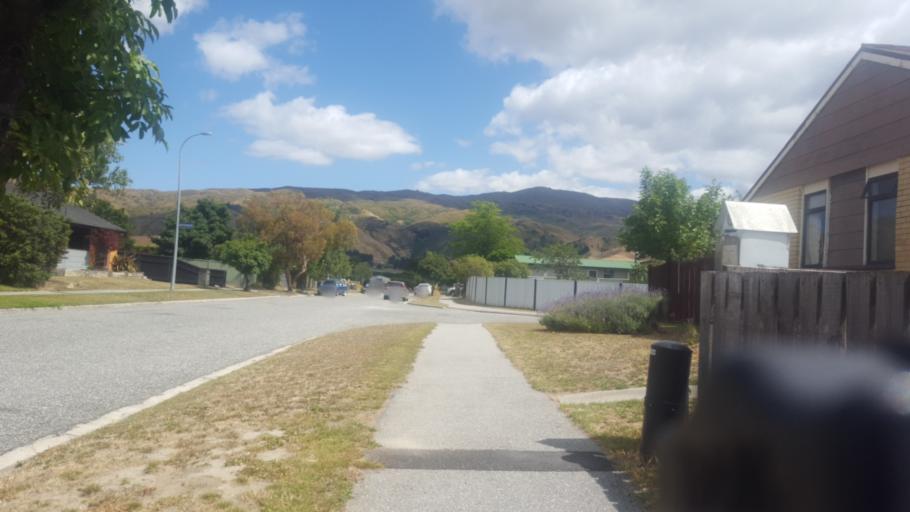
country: NZ
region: Otago
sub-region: Queenstown-Lakes District
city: Wanaka
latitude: -45.0420
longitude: 169.1835
